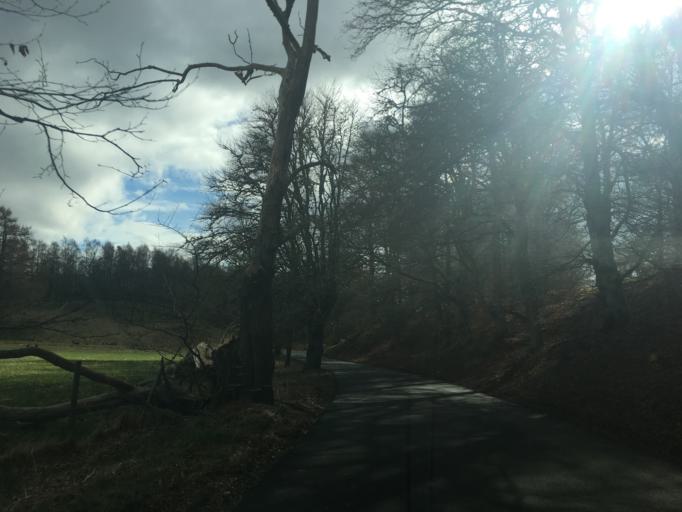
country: GB
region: Scotland
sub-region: Highland
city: Aviemore
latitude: 57.1722
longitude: -3.8240
